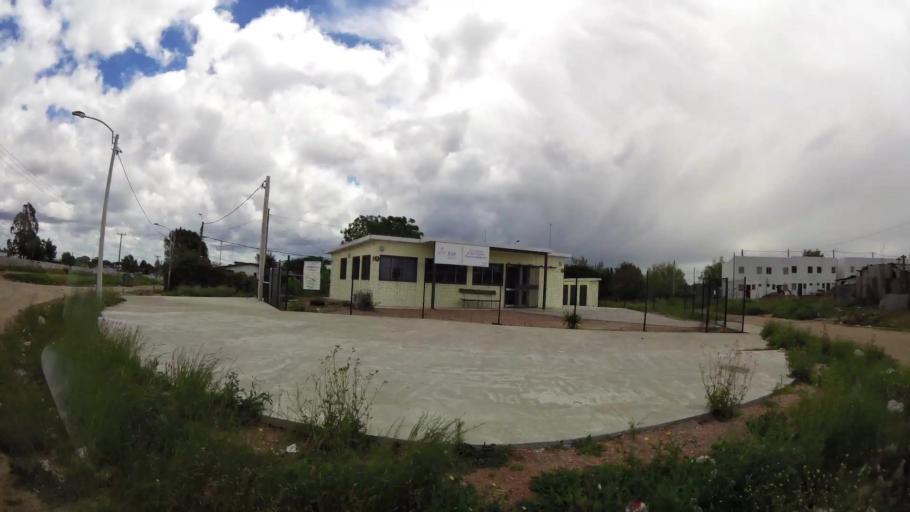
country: UY
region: Montevideo
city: Montevideo
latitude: -34.8228
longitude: -56.1648
